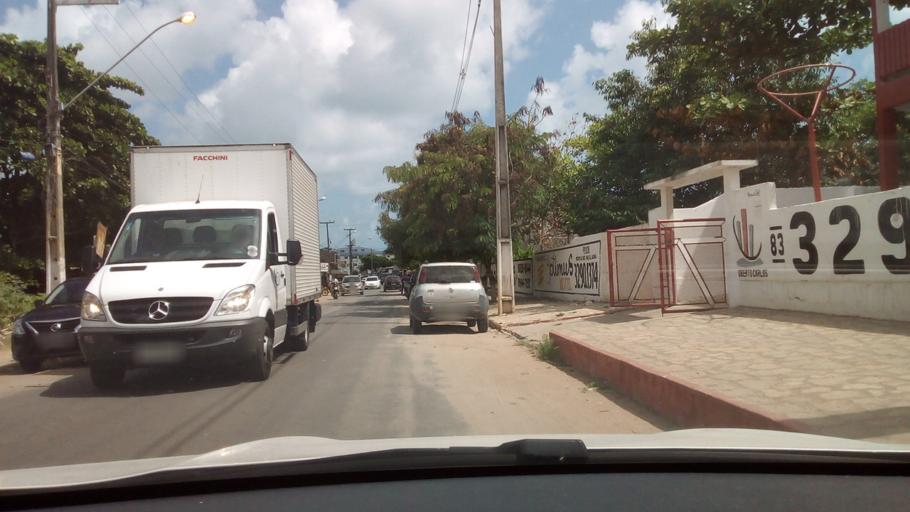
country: BR
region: Paraiba
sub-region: Conde
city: Conde
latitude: -7.2828
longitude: -34.8013
